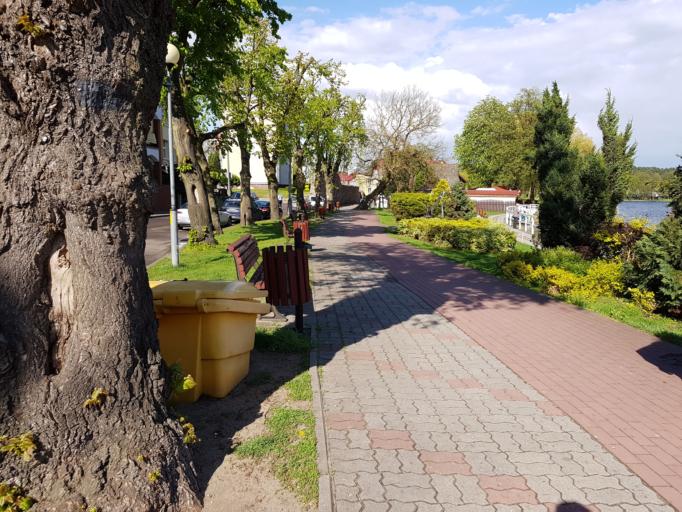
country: PL
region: West Pomeranian Voivodeship
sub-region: Powiat mysliborski
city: Barlinek
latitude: 52.9911
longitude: 15.2181
